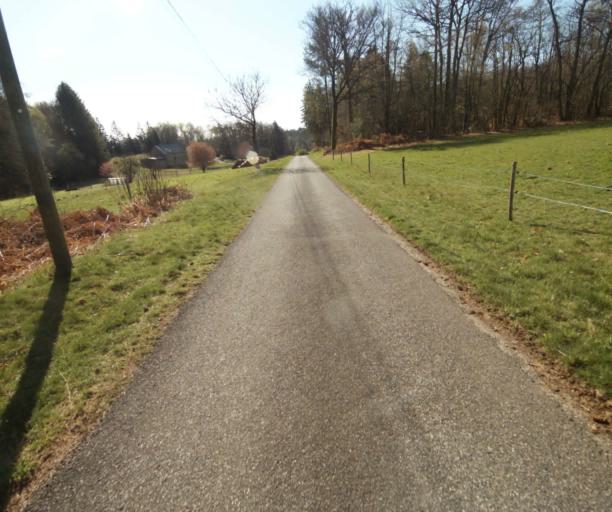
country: FR
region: Limousin
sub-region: Departement de la Correze
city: Laguenne
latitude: 45.2450
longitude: 1.9125
